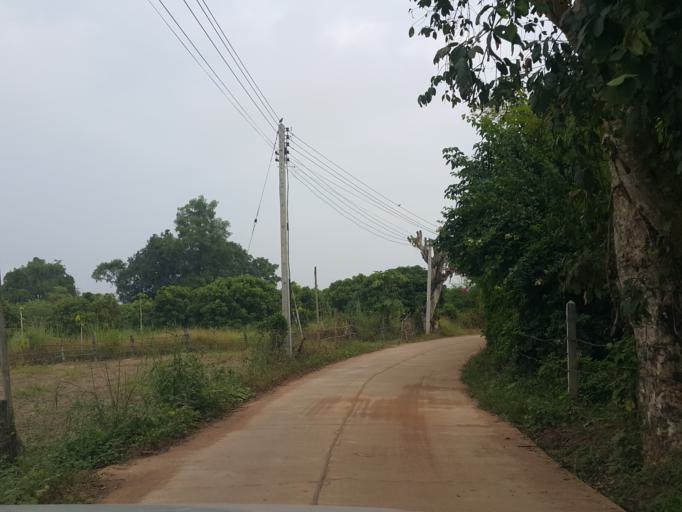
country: TH
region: Mae Hong Son
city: Wiang Nuea
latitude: 19.3749
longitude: 98.4512
